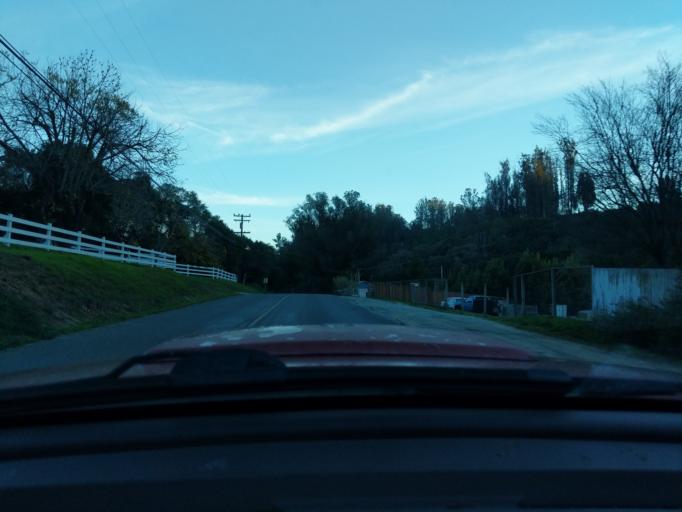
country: US
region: California
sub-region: San Benito County
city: Aromas
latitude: 36.8414
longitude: -121.6744
